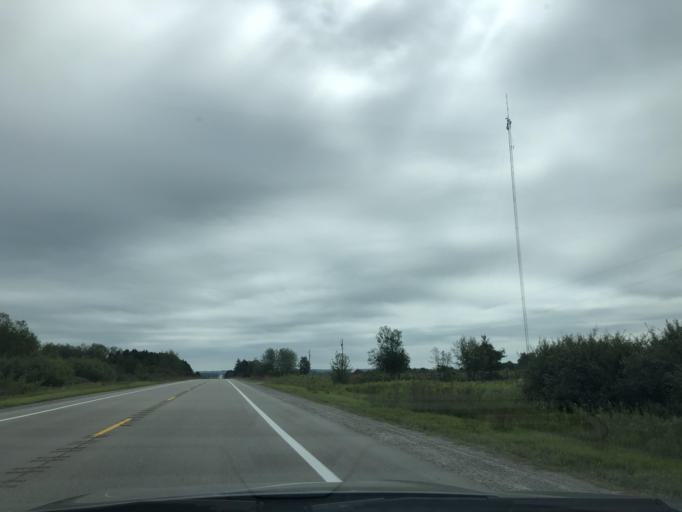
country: US
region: Michigan
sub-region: Clare County
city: Harrison
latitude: 44.0312
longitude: -84.9607
